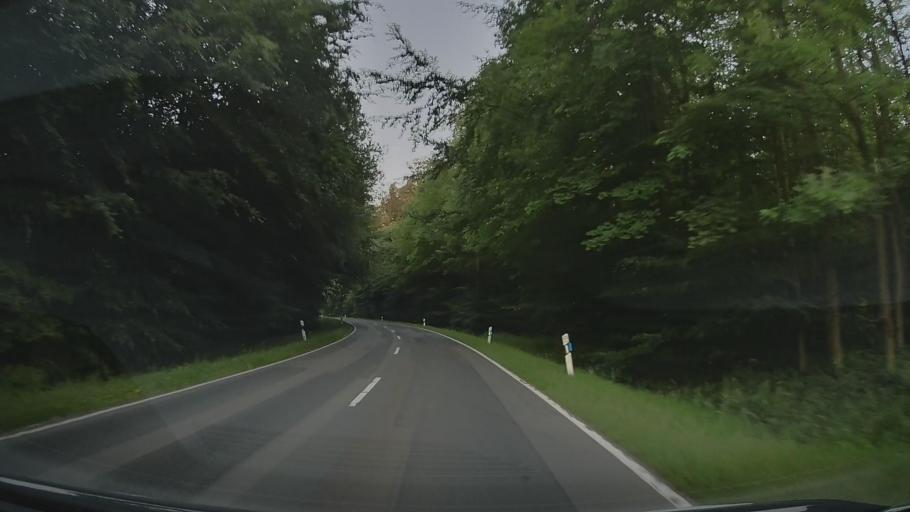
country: DE
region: Lower Saxony
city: Aerzen
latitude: 52.0261
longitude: 9.2805
